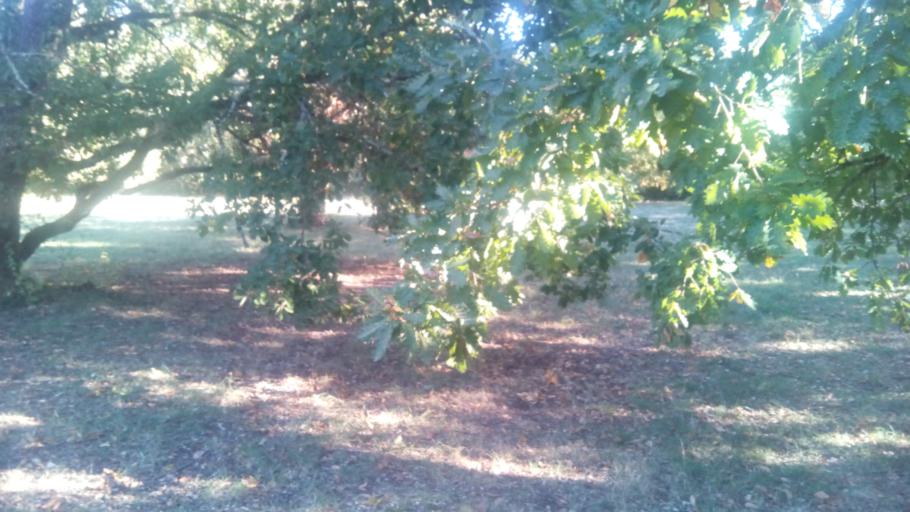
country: FR
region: Midi-Pyrenees
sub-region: Departement du Tarn-et-Garonne
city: Cazes-Mondenard
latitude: 44.2683
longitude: 1.2340
